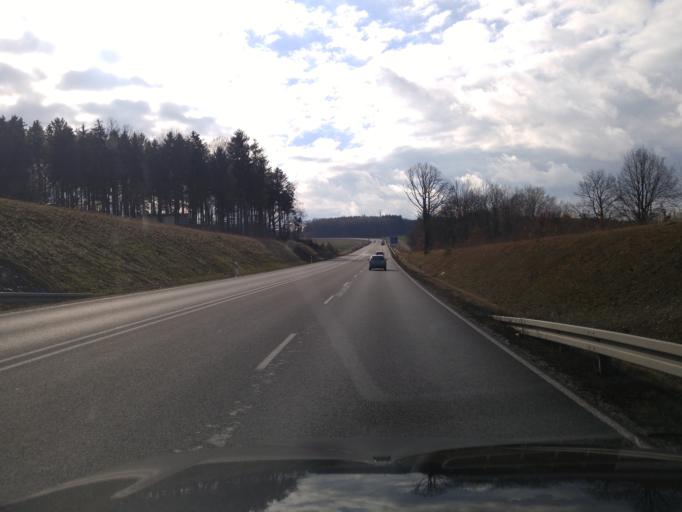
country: DE
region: Saxony
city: Hirschfeld
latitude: 50.6476
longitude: 12.4450
